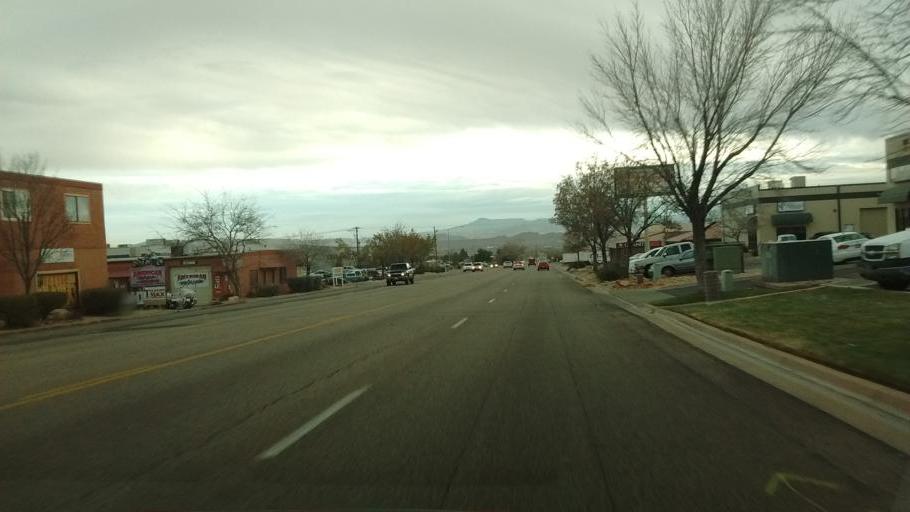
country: US
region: Utah
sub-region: Washington County
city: Washington
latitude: 37.1196
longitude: -113.5208
